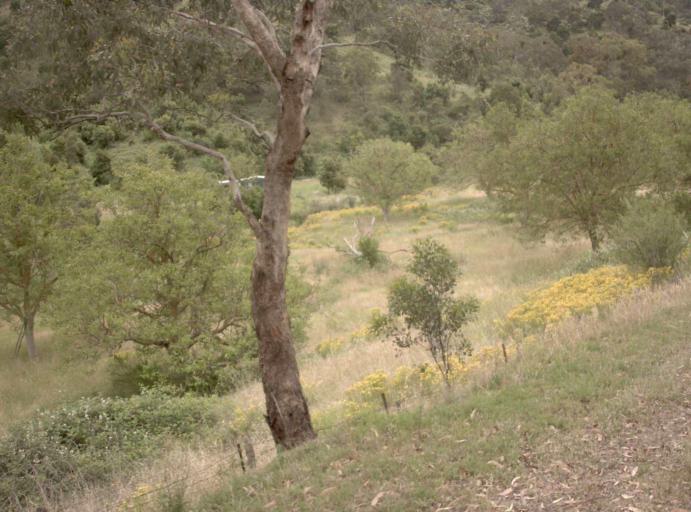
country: AU
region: Victoria
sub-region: East Gippsland
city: Bairnsdale
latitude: -37.5313
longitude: 147.2198
